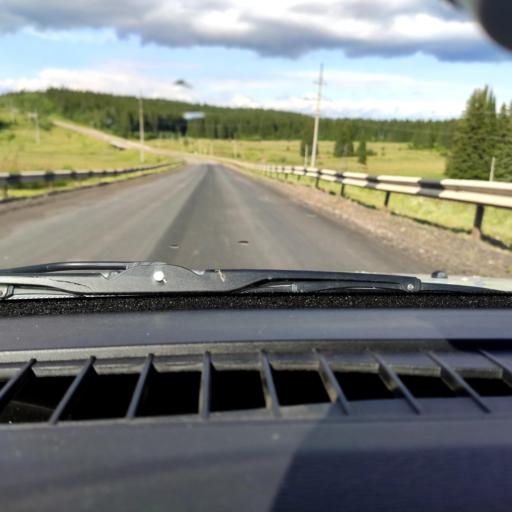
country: RU
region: Perm
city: Uinskoye
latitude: 57.1155
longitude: 56.5471
